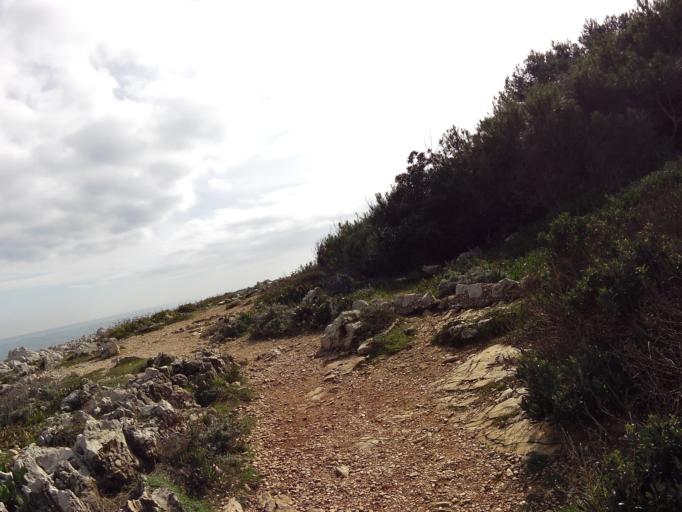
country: FR
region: Provence-Alpes-Cote d'Azur
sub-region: Departement des Alpes-Maritimes
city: Antibes
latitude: 43.5480
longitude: 7.1374
